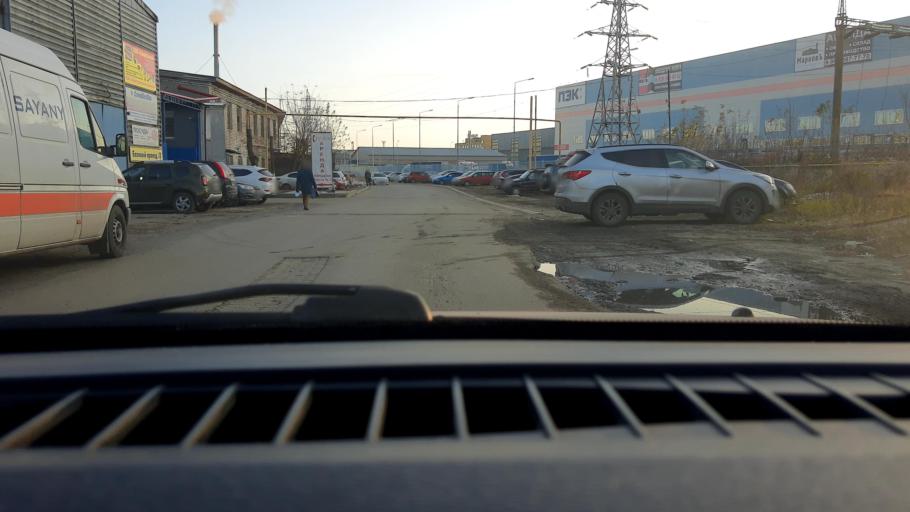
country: RU
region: Nizjnij Novgorod
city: Gorbatovka
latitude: 56.3064
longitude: 43.8659
